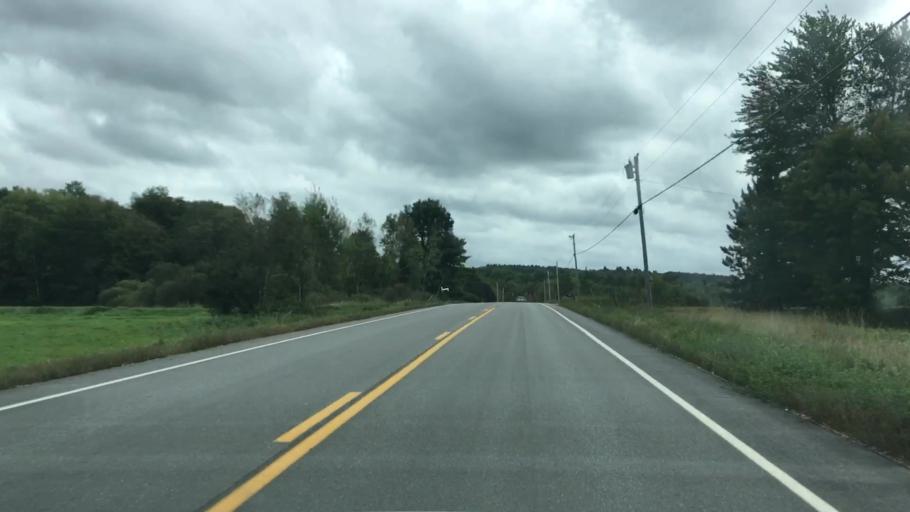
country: US
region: Maine
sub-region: Penobscot County
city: Hermon
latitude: 44.7489
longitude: -68.9689
